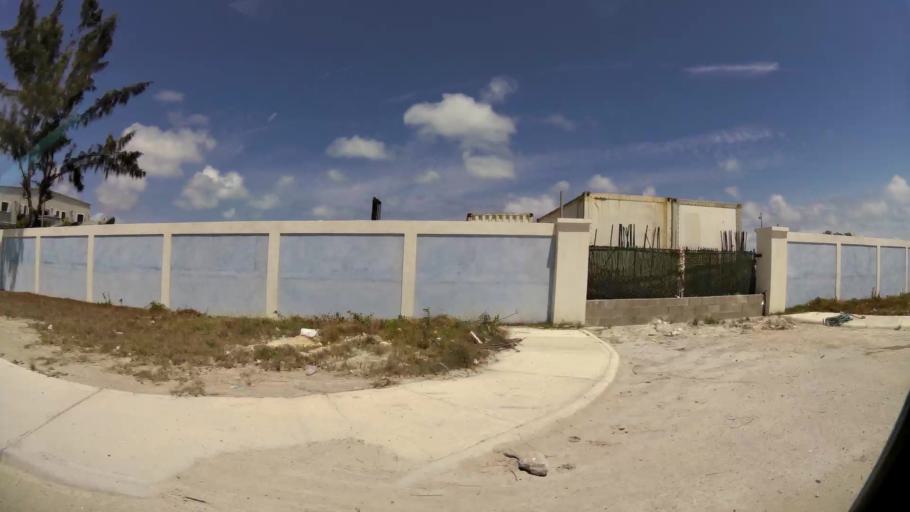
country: BS
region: Mayaguana
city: Abraham's Bay
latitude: 21.7710
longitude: -72.2553
